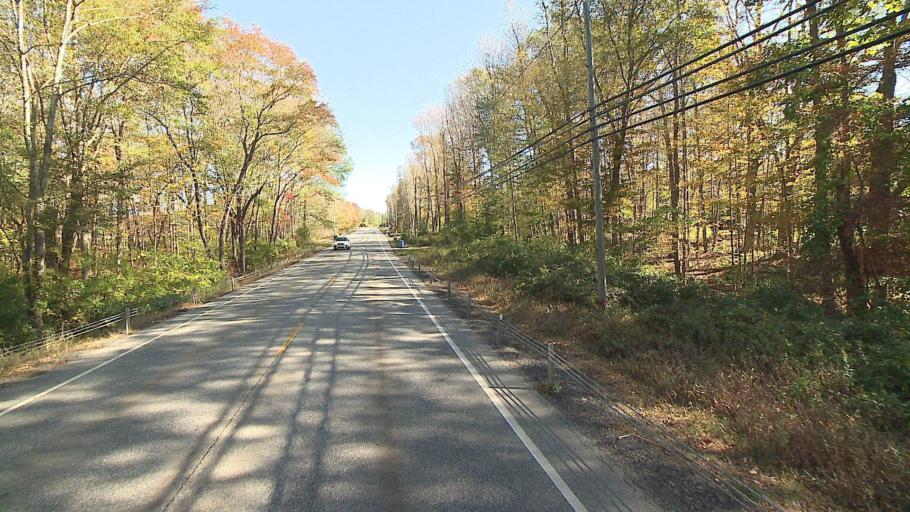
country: US
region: Connecticut
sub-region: Tolland County
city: Hebron
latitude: 41.6546
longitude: -72.3838
